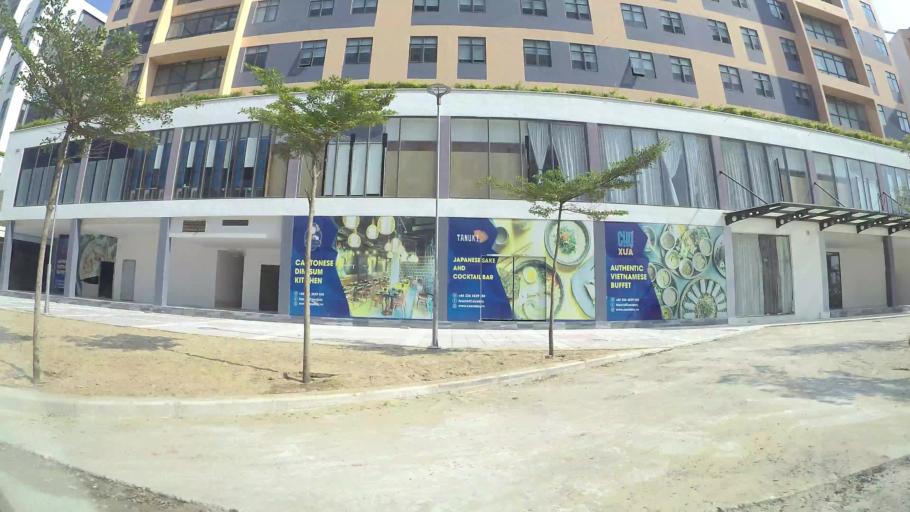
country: VN
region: Da Nang
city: Ngu Hanh Son
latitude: 15.9643
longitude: 108.2799
